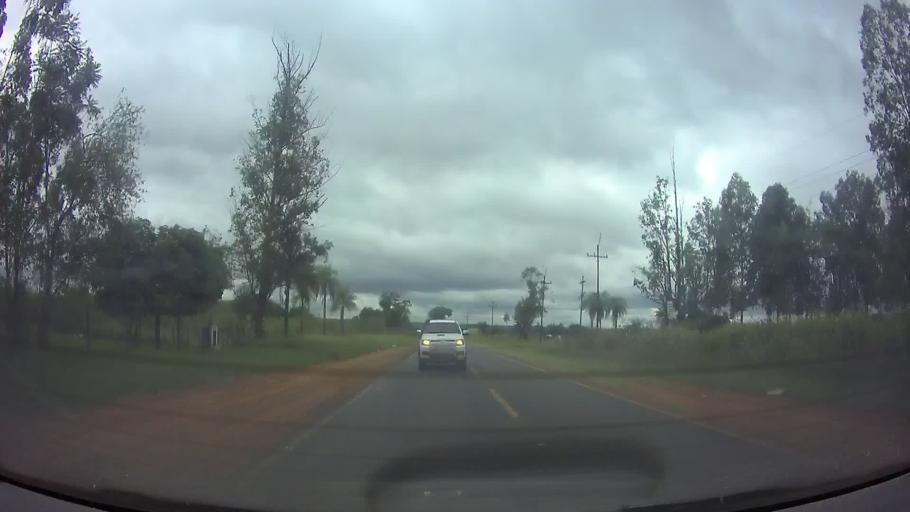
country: PY
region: Central
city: Guarambare
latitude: -25.5091
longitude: -57.4866
